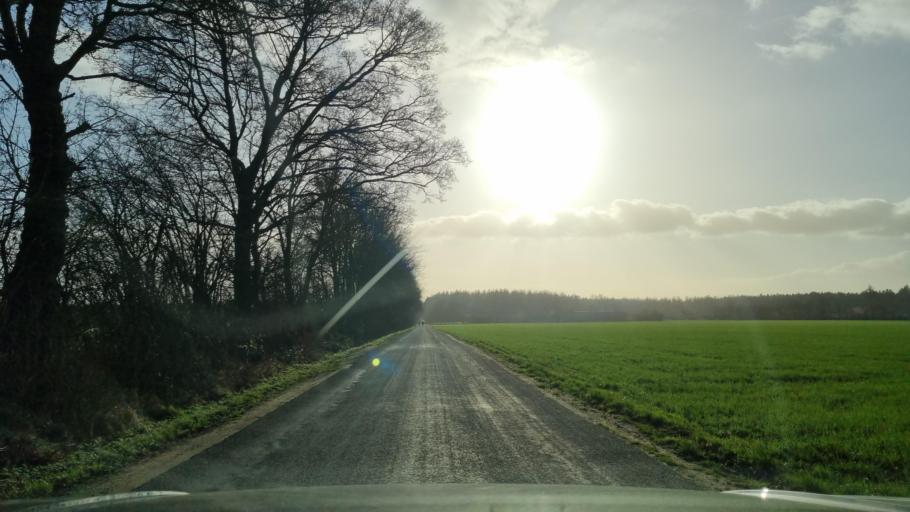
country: DE
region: North Rhine-Westphalia
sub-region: Regierungsbezirk Dusseldorf
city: Kleve
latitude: 51.7454
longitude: 6.1533
